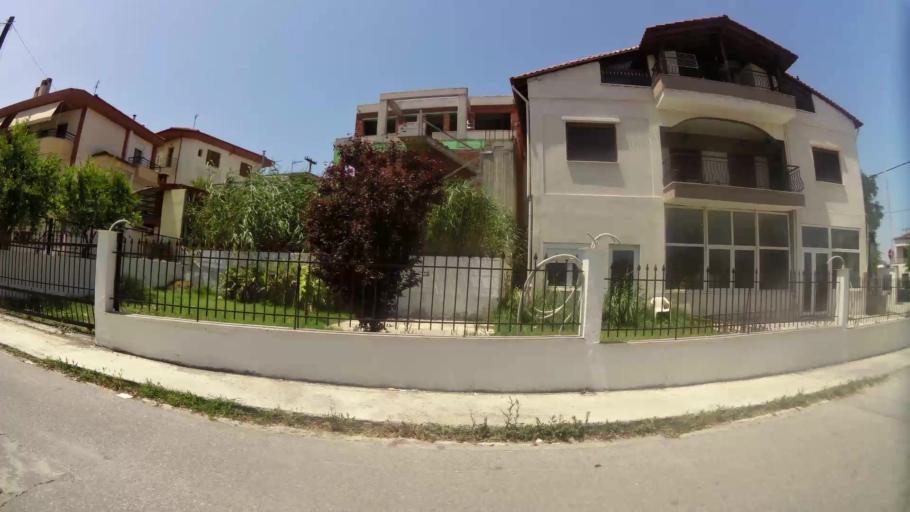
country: GR
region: Central Macedonia
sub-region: Nomos Thessalonikis
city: Plagiari
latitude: 40.4707
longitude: 22.9575
